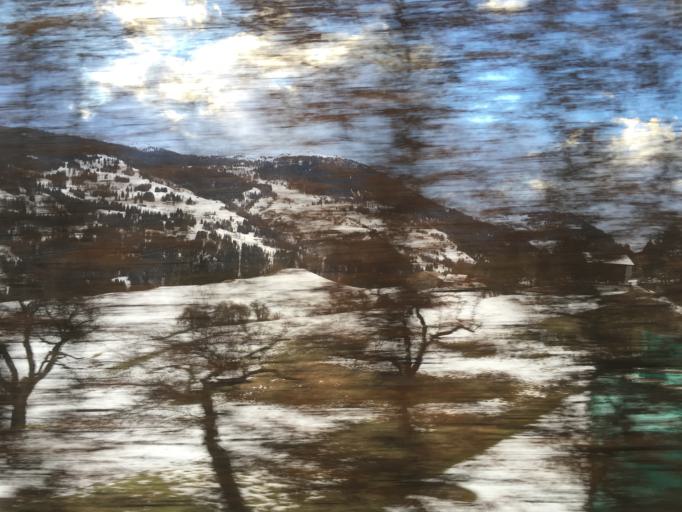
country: CH
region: Grisons
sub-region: Albula District
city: Tiefencastel
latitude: 46.6697
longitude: 9.5793
